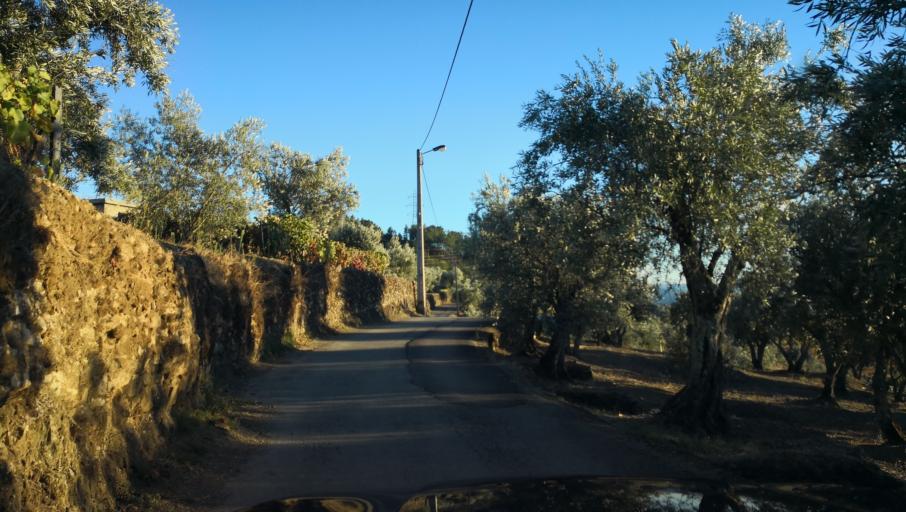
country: PT
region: Vila Real
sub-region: Santa Marta de Penaguiao
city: Santa Marta de Penaguiao
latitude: 41.2480
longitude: -7.7672
